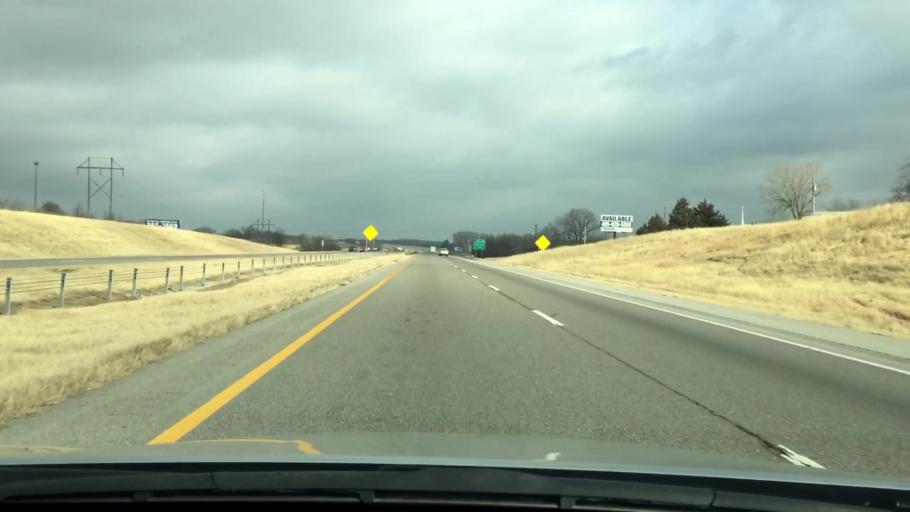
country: US
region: Oklahoma
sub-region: McClain County
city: Purcell
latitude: 35.0268
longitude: -97.3758
